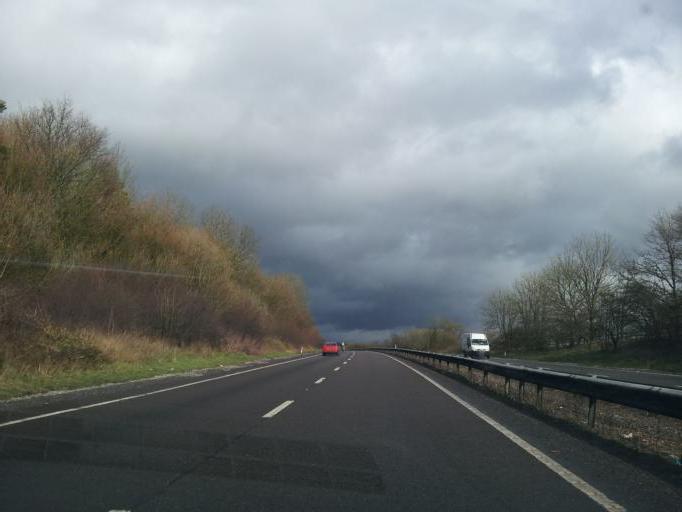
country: GB
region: England
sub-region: Somerset
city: Wincanton
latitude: 51.0425
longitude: -2.4551
